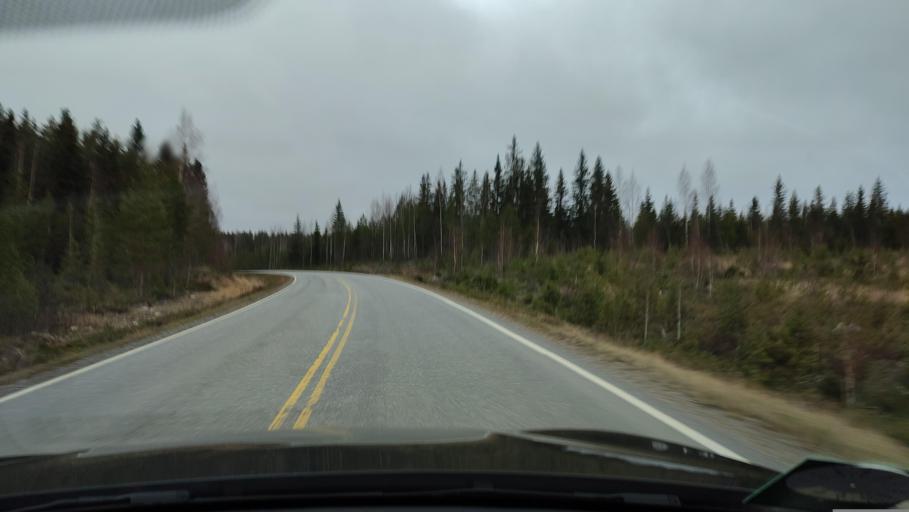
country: FI
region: Southern Ostrobothnia
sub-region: Suupohja
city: Karijoki
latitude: 62.2372
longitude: 21.7574
